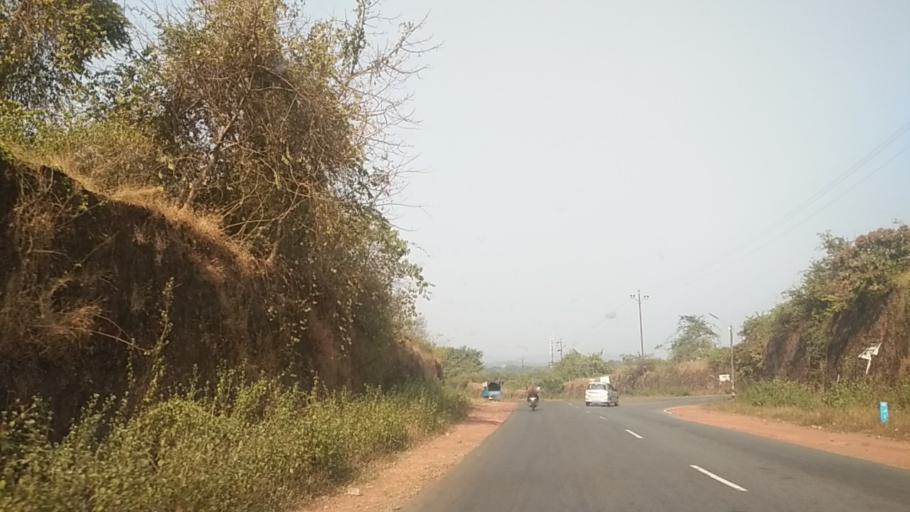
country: IN
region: Goa
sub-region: North Goa
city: Colovale
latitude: 15.6371
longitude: 73.8311
